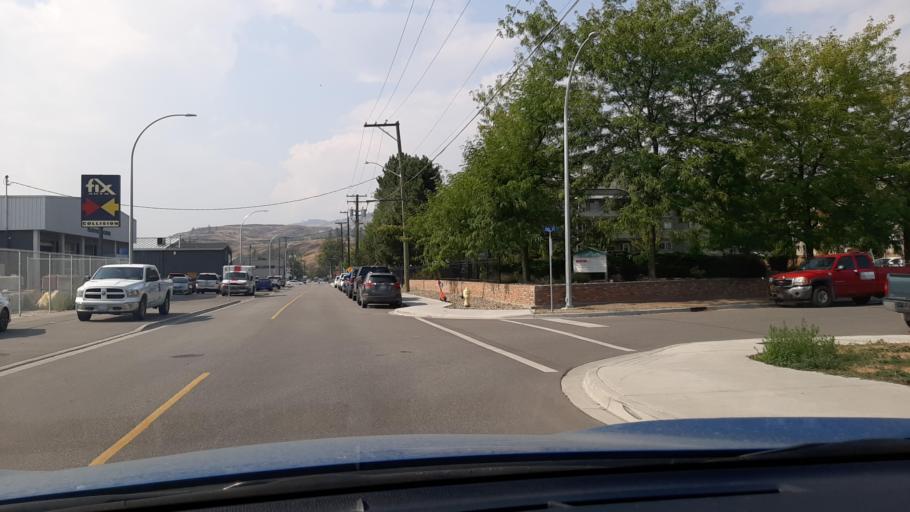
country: CA
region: British Columbia
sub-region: Regional District of North Okanagan
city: Vernon
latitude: 50.2688
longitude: -119.2693
